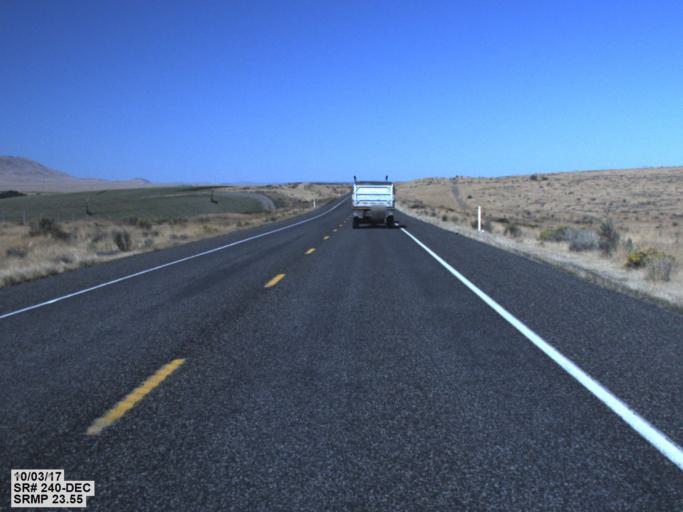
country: US
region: Washington
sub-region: Benton County
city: West Richland
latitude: 46.3557
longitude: -119.3722
